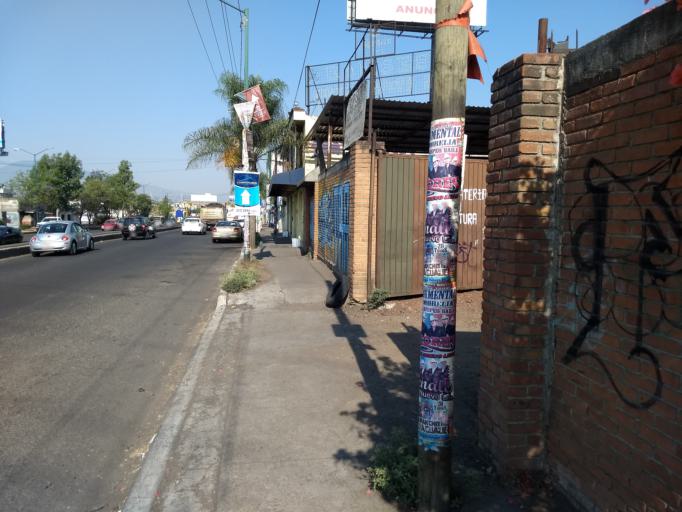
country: MX
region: Michoacan
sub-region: Morelia
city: San Antonio
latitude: 19.6993
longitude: -101.2483
